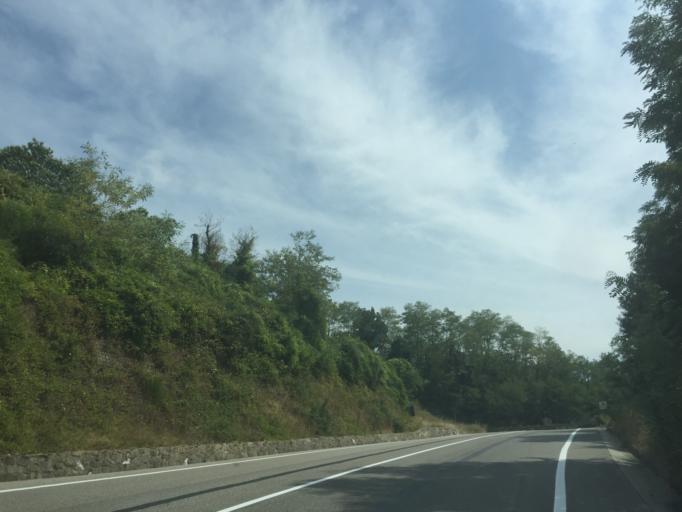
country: IT
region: Tuscany
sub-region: Provincia di Pistoia
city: Campo Tizzoro
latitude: 43.9876
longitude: 10.8557
